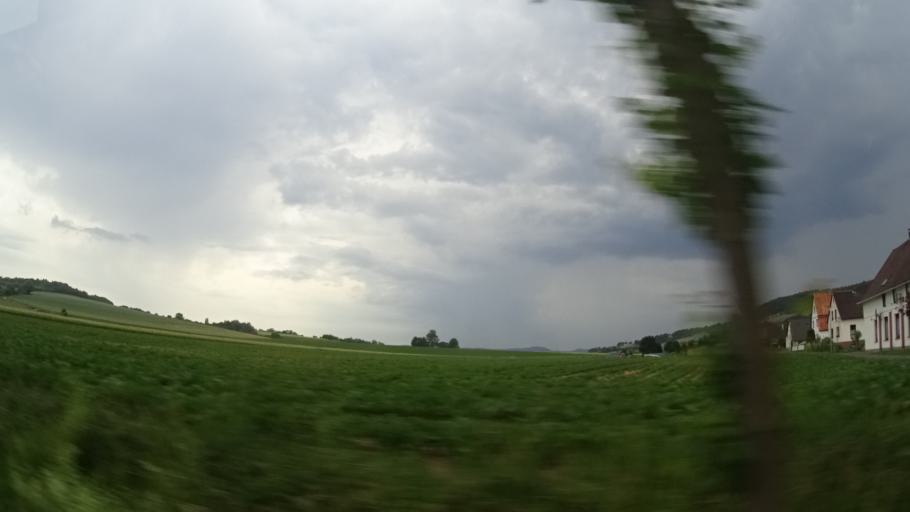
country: DE
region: Lower Saxony
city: Pegestorf
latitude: 51.9285
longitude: 9.4695
